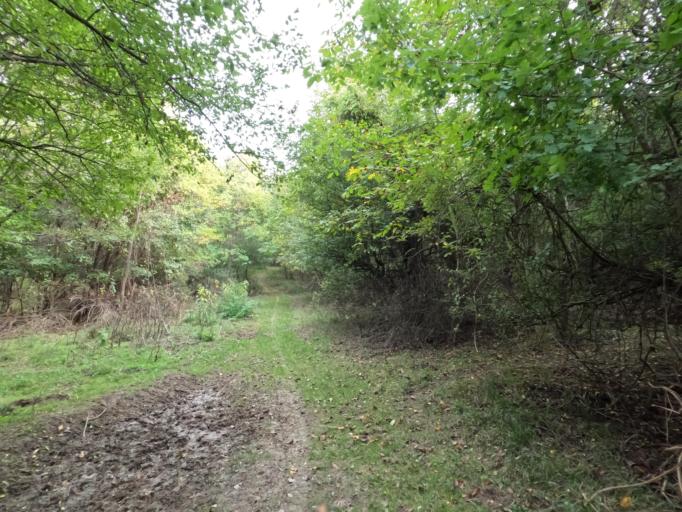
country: HU
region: Tolna
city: Szentgalpuszta
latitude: 46.3257
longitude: 18.6559
